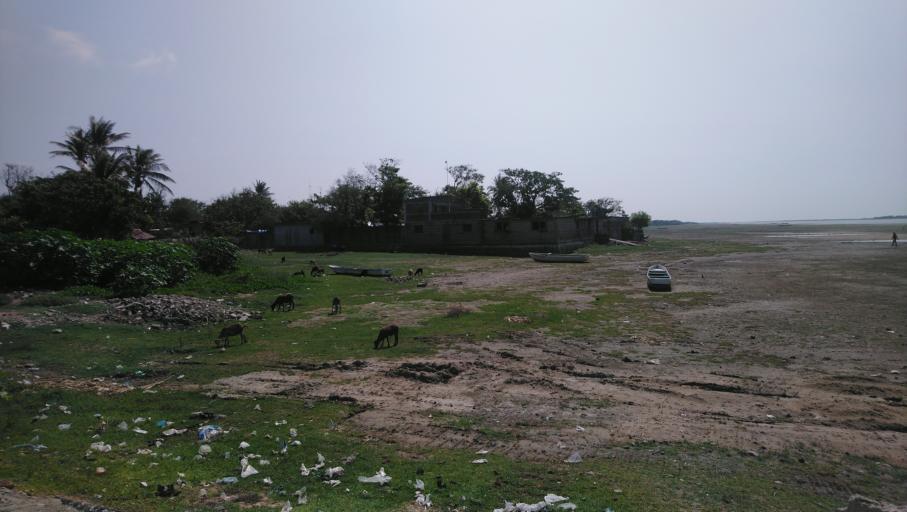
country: MX
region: Oaxaca
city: San Mateo del Mar
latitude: 16.2082
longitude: -94.9826
